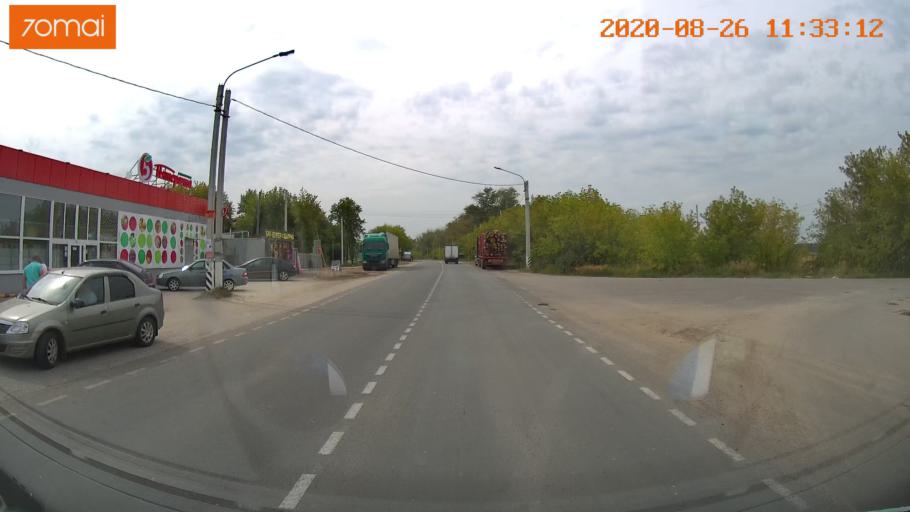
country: RU
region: Rjazan
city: Shilovo
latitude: 54.2979
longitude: 40.8565
